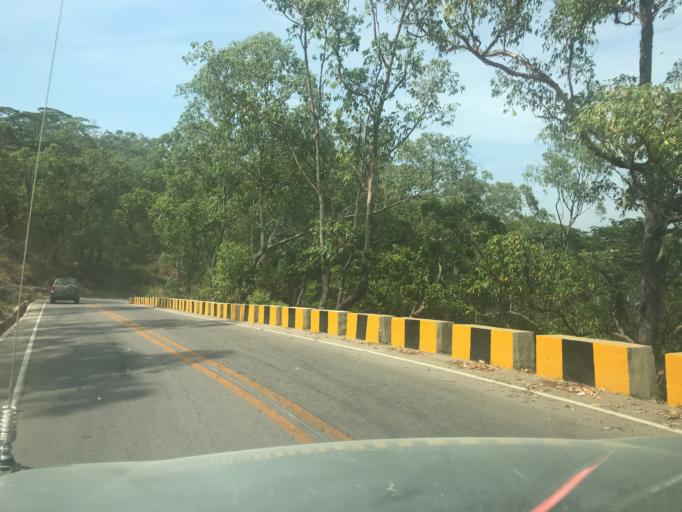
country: TL
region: Aileu
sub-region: Aileu Villa
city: Aileu
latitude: -8.6666
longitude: 125.5583
